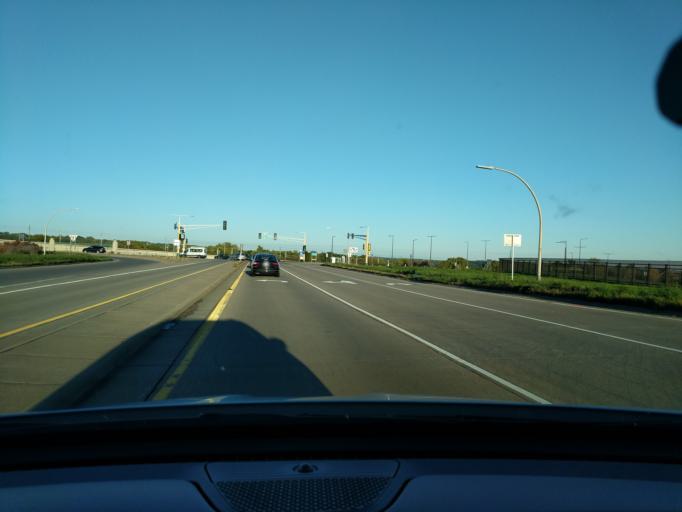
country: US
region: Minnesota
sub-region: Dakota County
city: Mendota Heights
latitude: 44.8974
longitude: -93.2012
